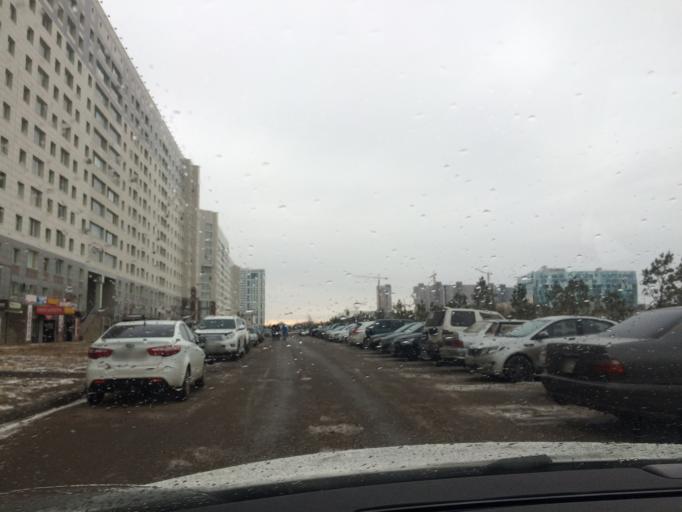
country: KZ
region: Astana Qalasy
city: Astana
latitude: 51.1221
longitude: 71.4144
